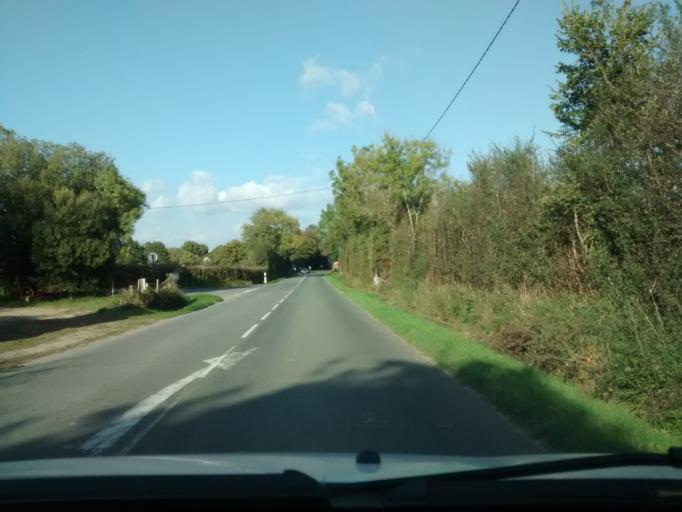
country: FR
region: Pays de la Loire
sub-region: Departement de la Loire-Atlantique
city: Coueron
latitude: 47.2368
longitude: -1.7008
